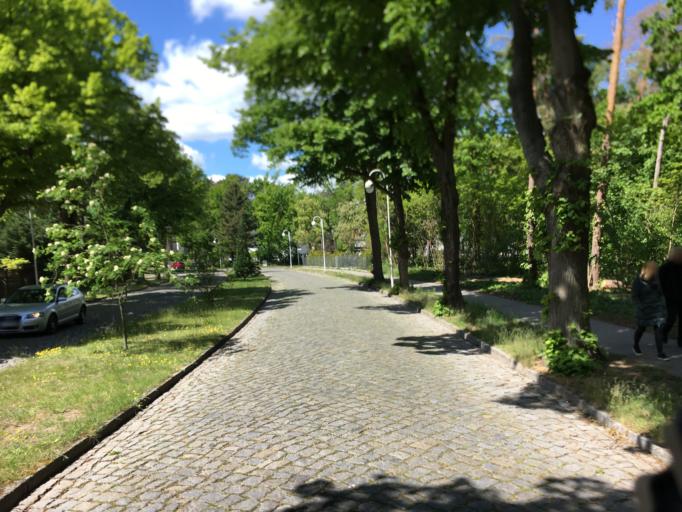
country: DE
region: Berlin
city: Lichtenrade
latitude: 52.3600
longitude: 13.4226
